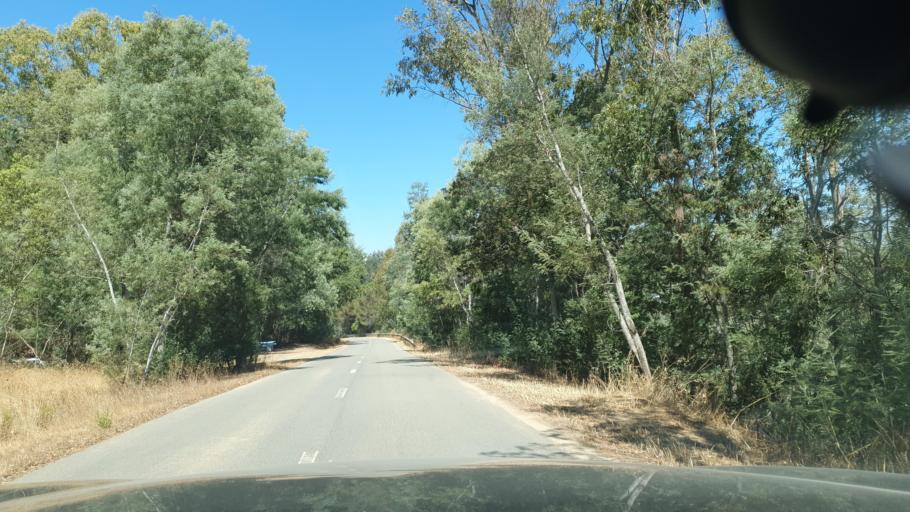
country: PT
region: Beja
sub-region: Odemira
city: Odemira
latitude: 37.5062
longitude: -8.4378
